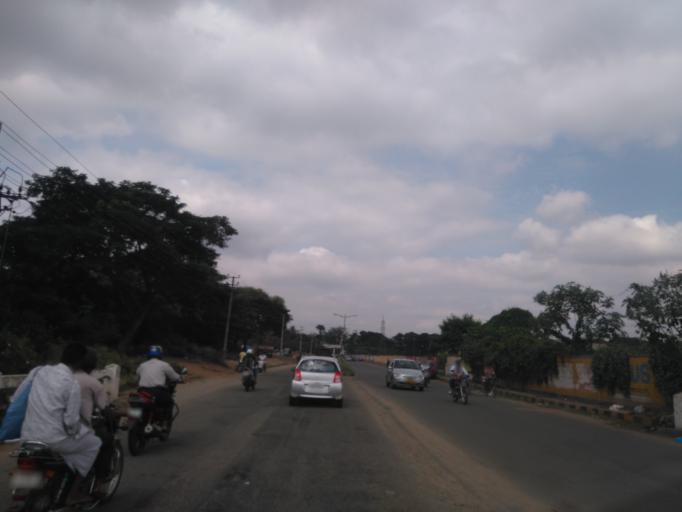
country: IN
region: Karnataka
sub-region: Mysore
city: Mysore
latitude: 12.2979
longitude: 76.6612
